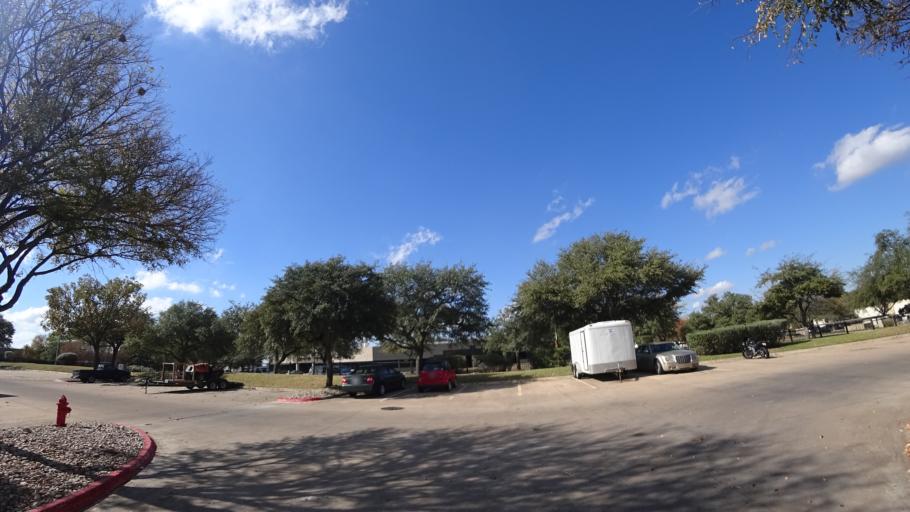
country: US
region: Texas
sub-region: Travis County
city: Wells Branch
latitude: 30.4395
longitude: -97.6911
